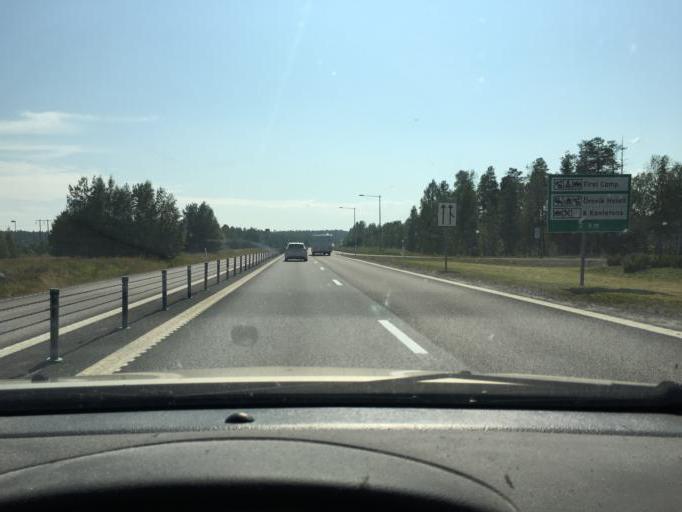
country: SE
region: Norrbotten
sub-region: Lulea Kommun
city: Gammelstad
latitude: 65.6149
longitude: 22.0564
